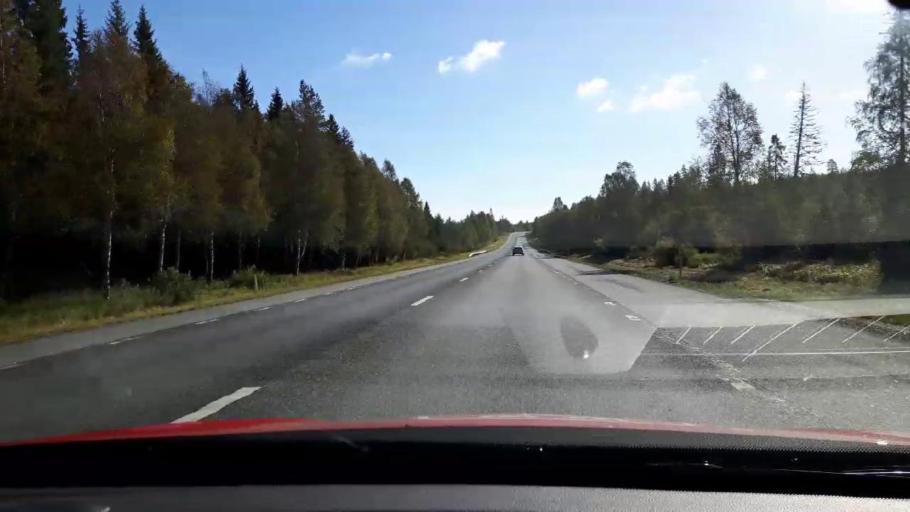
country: SE
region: Jaemtland
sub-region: Braecke Kommun
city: Braecke
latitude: 62.6886
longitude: 15.5600
